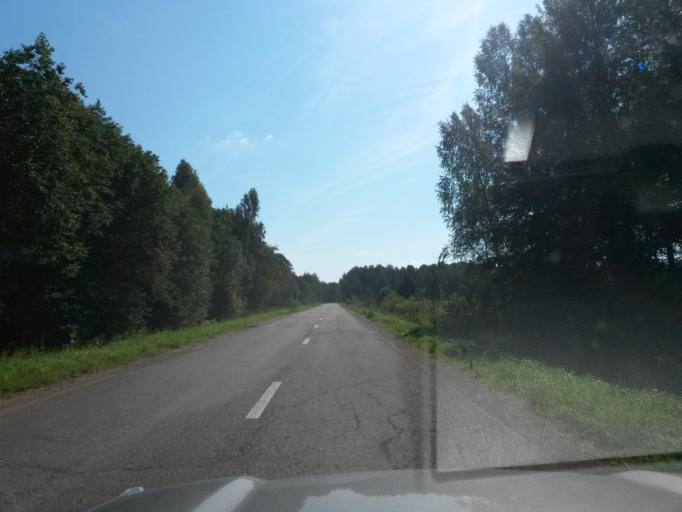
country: RU
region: Jaroslavl
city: Gavrilov-Yam
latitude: 57.3015
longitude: 40.0337
